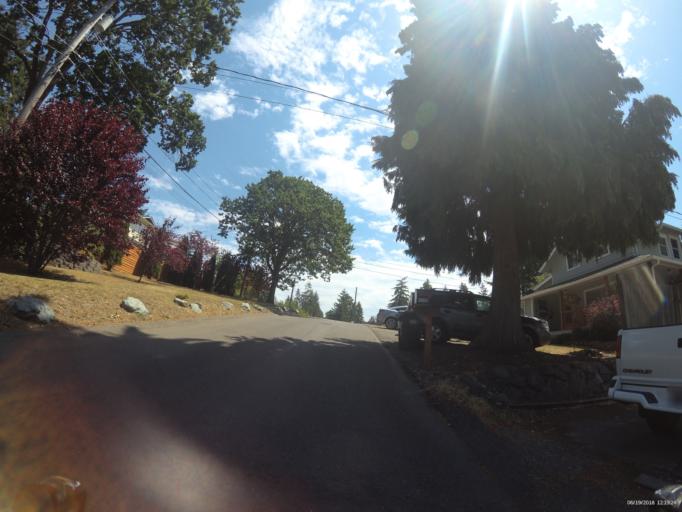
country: US
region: Washington
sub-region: Pierce County
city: Lakewood
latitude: 47.1751
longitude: -122.5336
